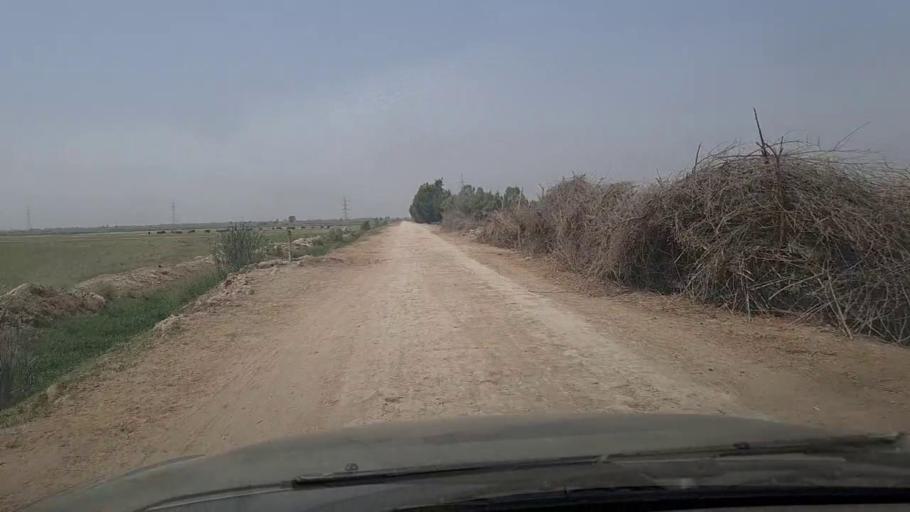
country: PK
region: Sindh
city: Adilpur
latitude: 27.9388
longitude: 69.3004
